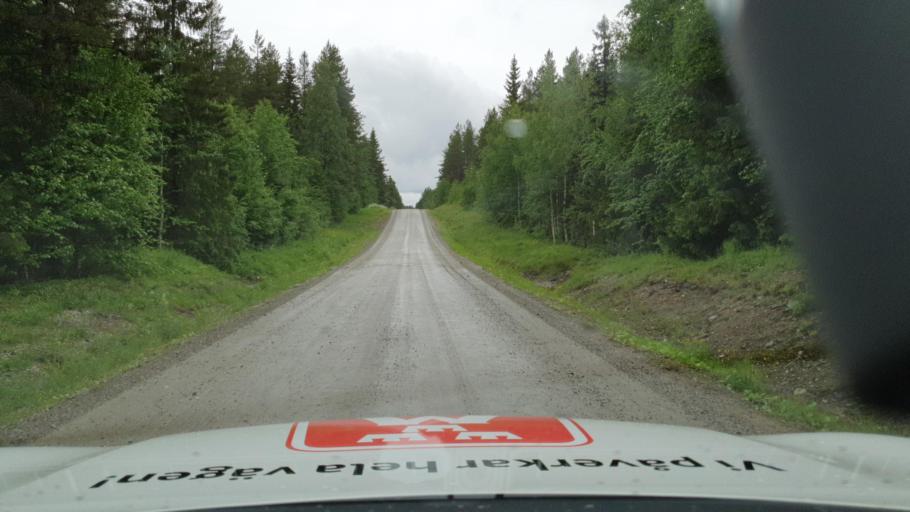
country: SE
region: Vaesterbotten
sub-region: Dorotea Kommun
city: Dorotea
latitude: 64.0632
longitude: 16.7110
